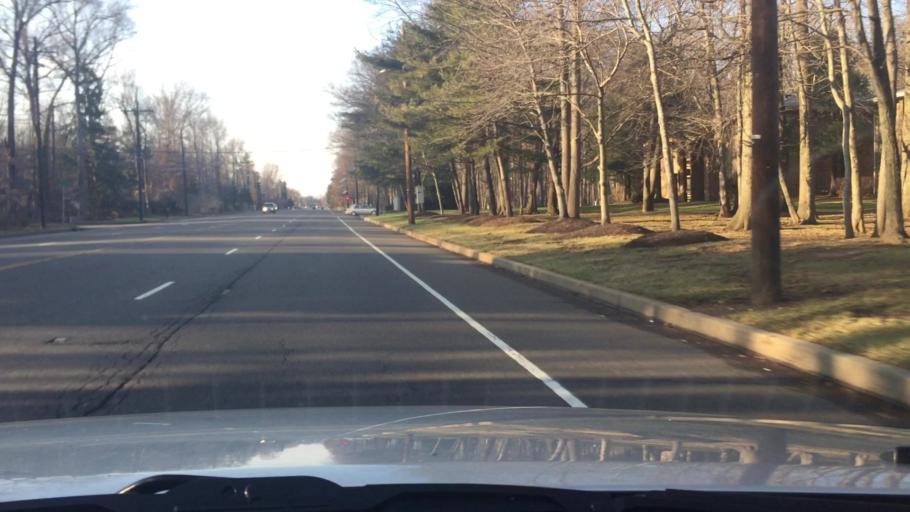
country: US
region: New Jersey
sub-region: Middlesex County
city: Kendall Park
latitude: 40.4353
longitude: -74.5217
